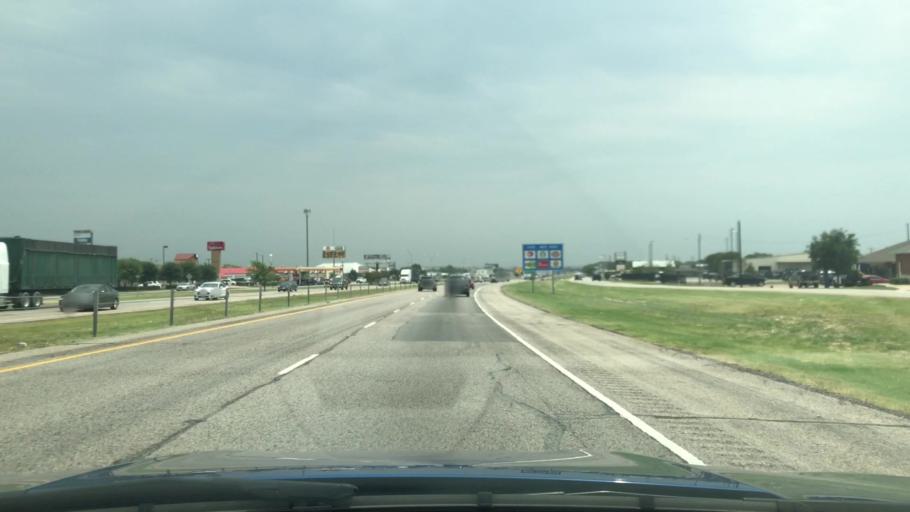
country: US
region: Texas
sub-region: Kaufman County
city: Forney
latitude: 32.7555
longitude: -96.4670
